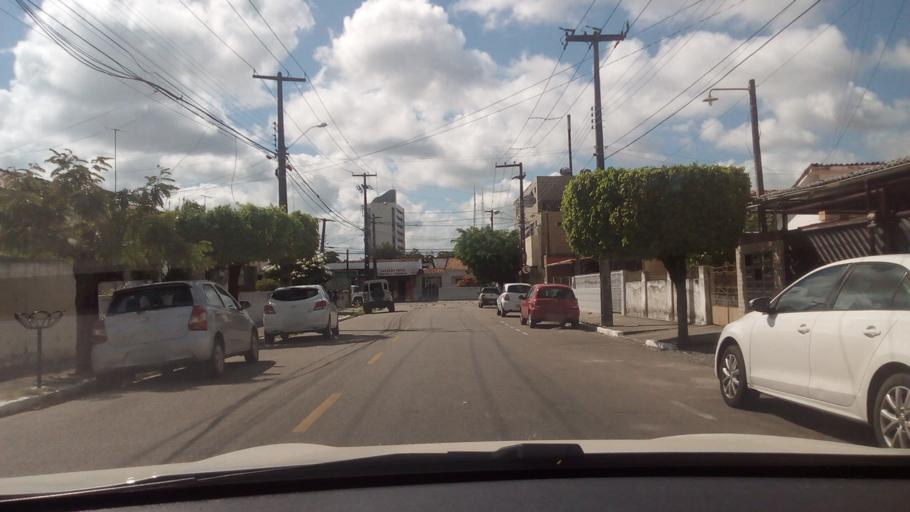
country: BR
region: Paraiba
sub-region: Joao Pessoa
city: Joao Pessoa
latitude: -7.1267
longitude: -34.8704
